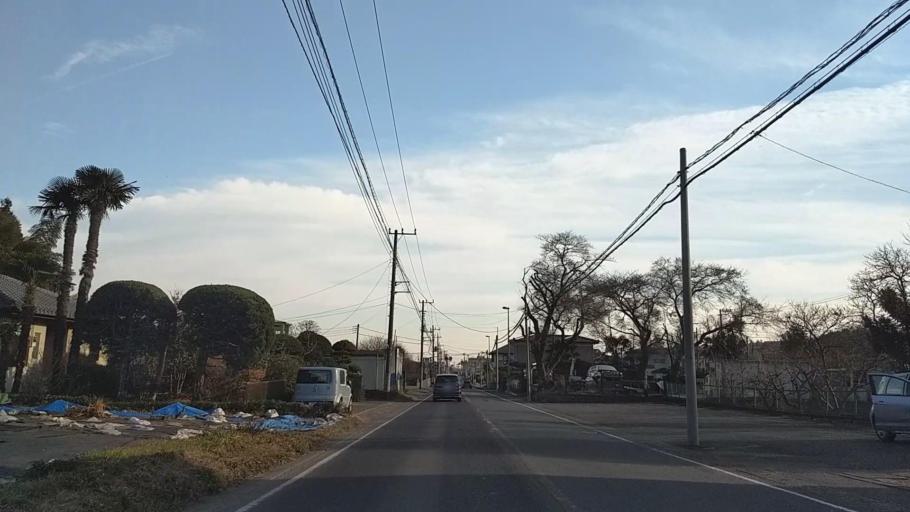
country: JP
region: Kanagawa
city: Zama
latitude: 35.5159
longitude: 139.2970
